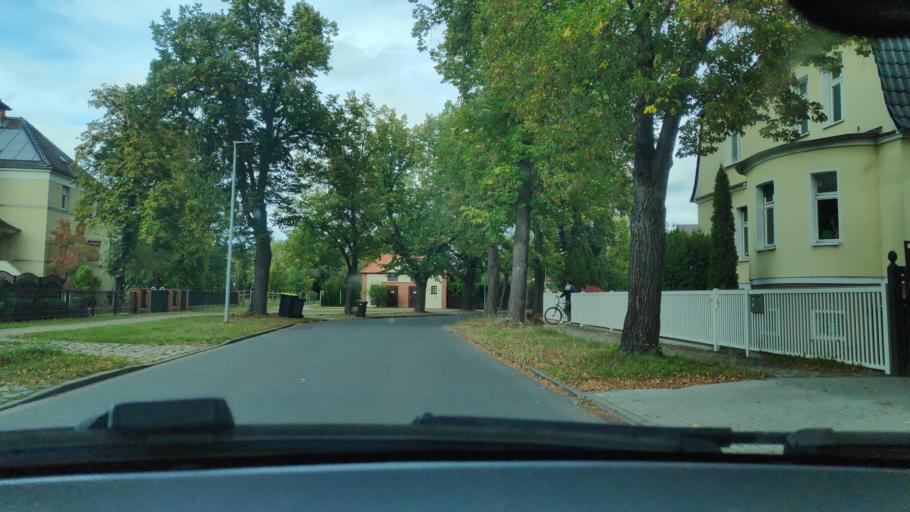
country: DE
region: Saxony-Anhalt
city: Biederitz
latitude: 52.1543
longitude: 11.7137
